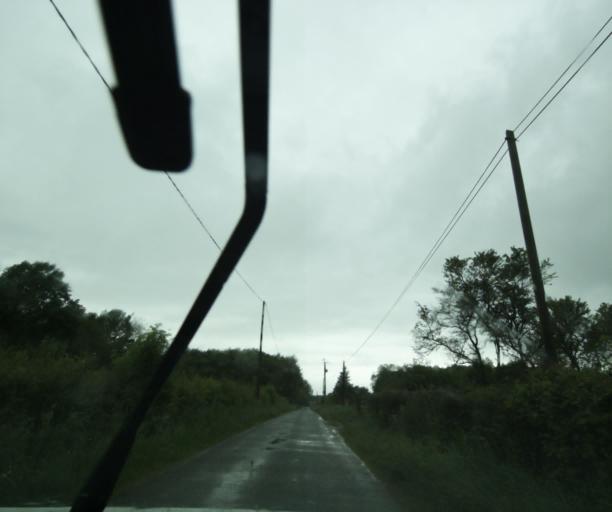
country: FR
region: Bourgogne
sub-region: Departement de Saone-et-Loire
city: Ciry-le-Noble
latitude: 46.5301
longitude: 4.3033
